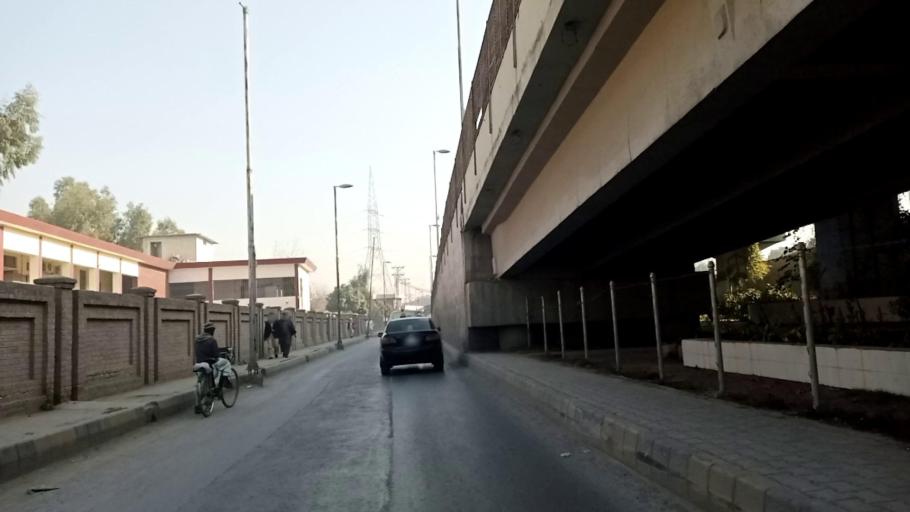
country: PK
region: Khyber Pakhtunkhwa
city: Peshawar
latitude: 34.0157
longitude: 71.5688
